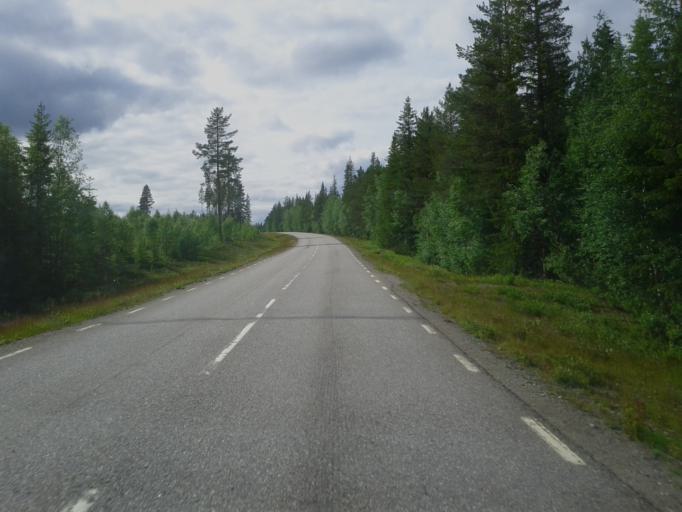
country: SE
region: Vaesterbotten
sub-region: Sorsele Kommun
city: Sorsele
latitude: 65.2850
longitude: 17.8554
